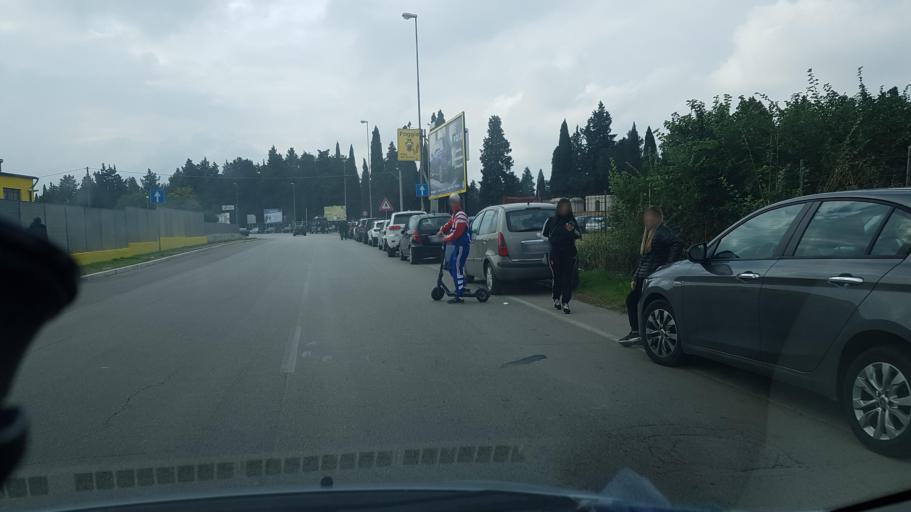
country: IT
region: Apulia
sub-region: Provincia di Foggia
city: Foggia
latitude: 41.4741
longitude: 15.5503
